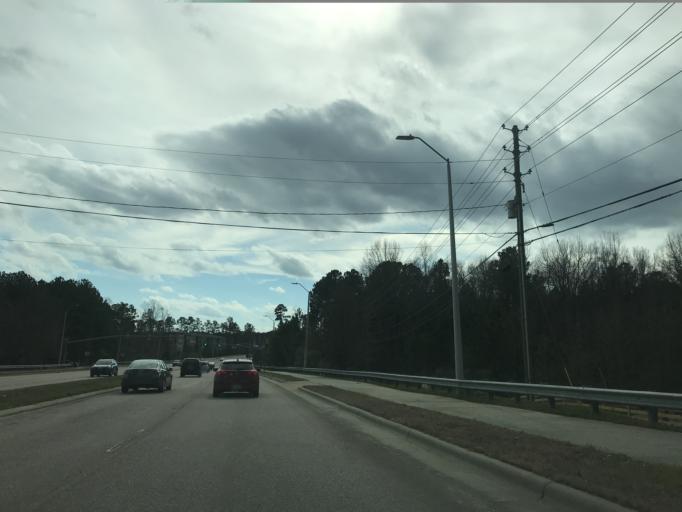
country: US
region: North Carolina
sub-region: Wake County
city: Morrisville
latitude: 35.8184
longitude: -78.8478
